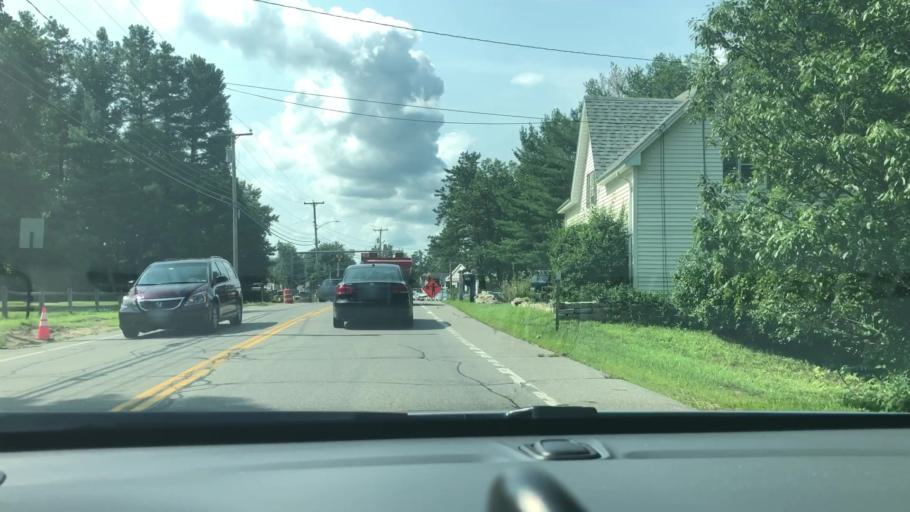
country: US
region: New Hampshire
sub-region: Hillsborough County
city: Pinardville
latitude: 43.0111
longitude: -71.5460
